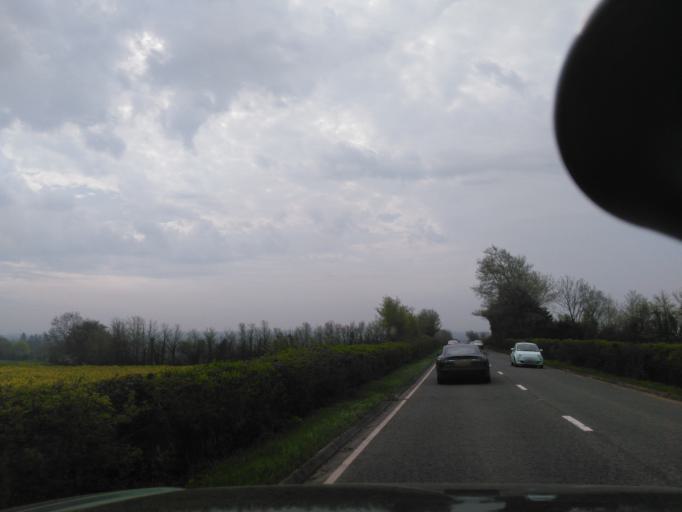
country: GB
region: England
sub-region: Bath and North East Somerset
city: Hinton Charterhouse
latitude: 51.2961
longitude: -2.3036
